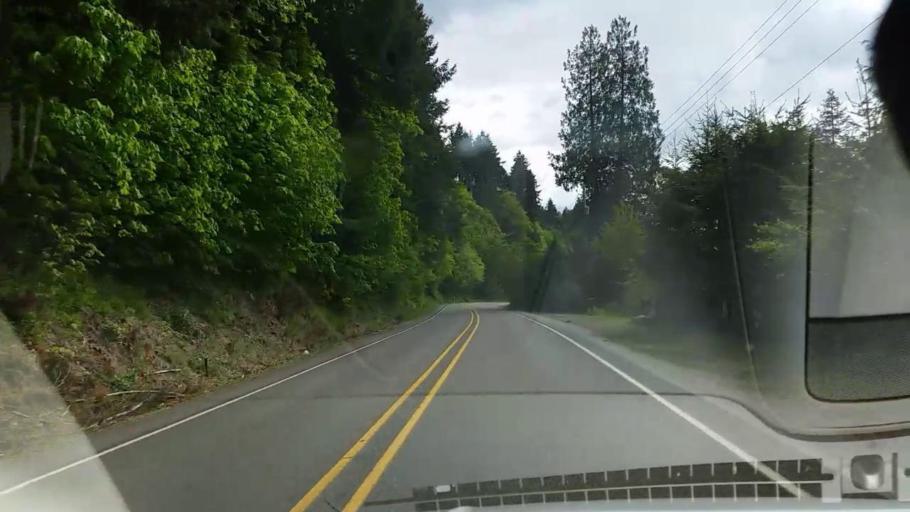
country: US
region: Washington
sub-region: Mason County
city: Shelton
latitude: 47.3412
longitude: -123.1098
